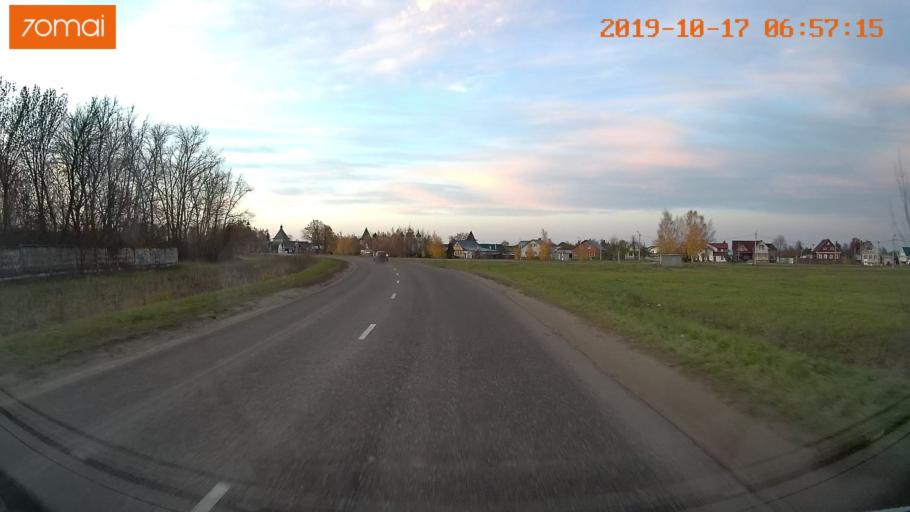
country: RU
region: Vladimir
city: Suzdal'
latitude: 56.4381
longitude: 40.4408
